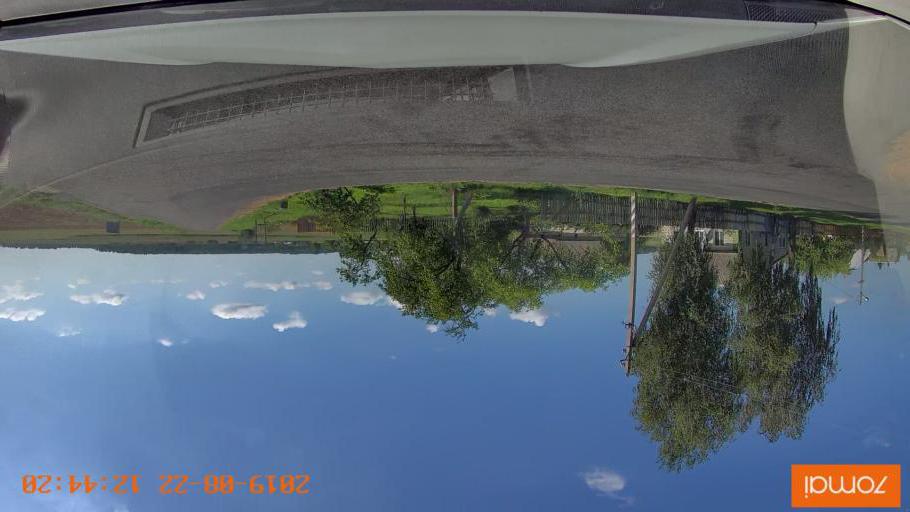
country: BY
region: Minsk
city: Prawdzinski
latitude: 53.4495
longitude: 27.6097
